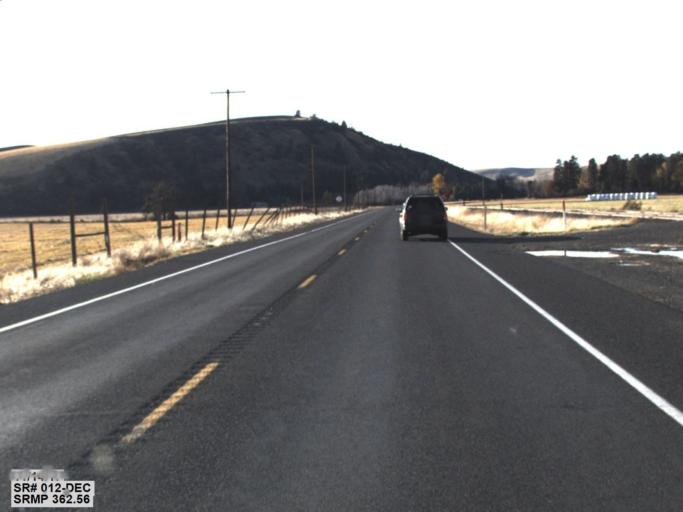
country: US
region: Washington
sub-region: Columbia County
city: Dayton
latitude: 46.2870
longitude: -118.0591
